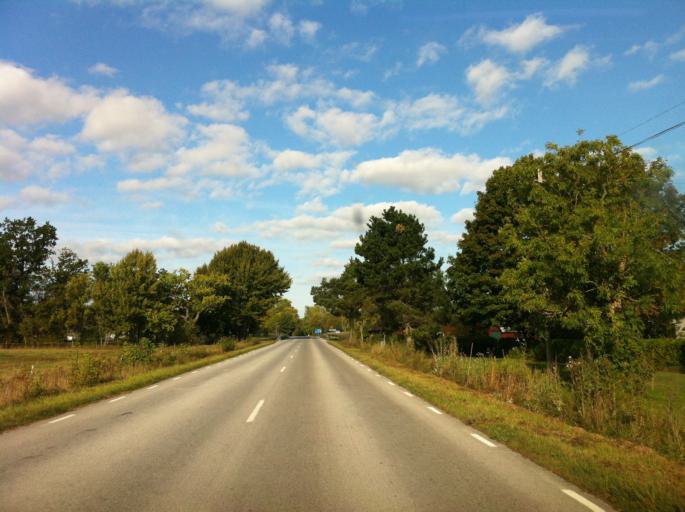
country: SE
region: Gotland
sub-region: Gotland
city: Slite
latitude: 57.4436
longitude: 18.7217
